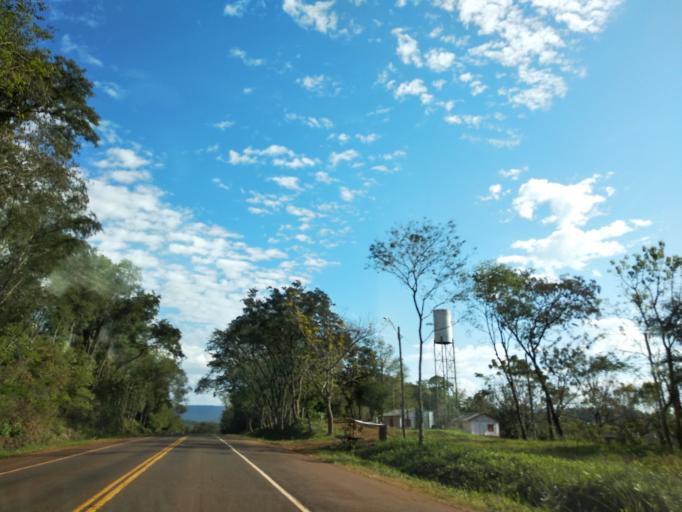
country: AR
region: Misiones
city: Aristobulo del Valle
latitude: -27.0974
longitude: -54.9571
